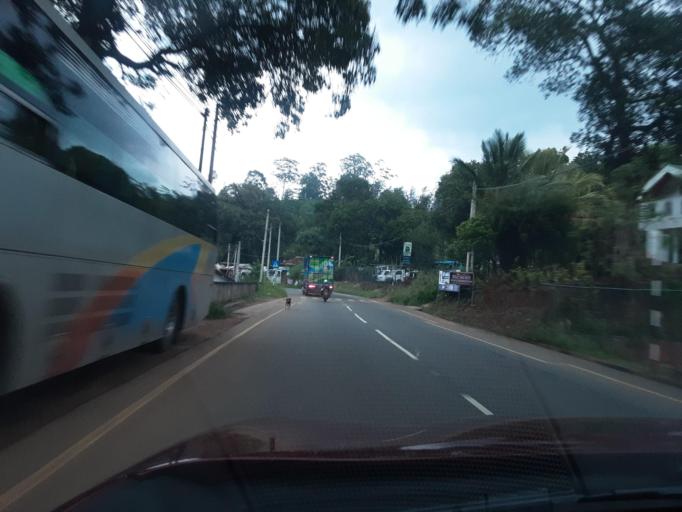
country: LK
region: Central
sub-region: Nuwara Eliya District
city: Nuwara Eliya
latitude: 6.9023
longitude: 80.8968
